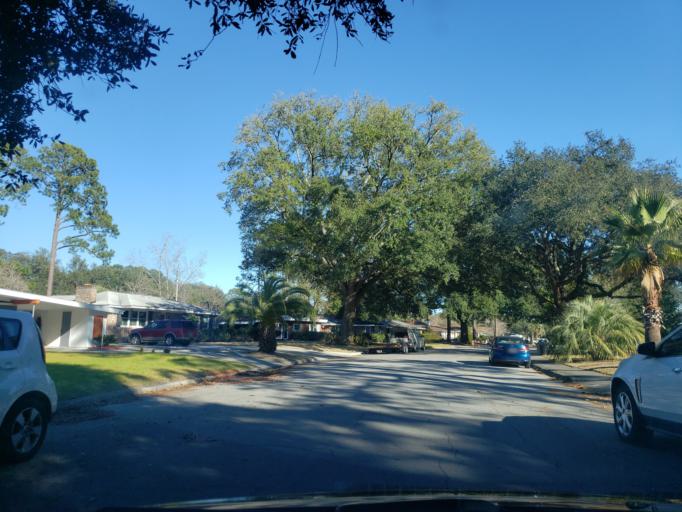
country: US
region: Georgia
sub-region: Chatham County
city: Thunderbolt
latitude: 32.0229
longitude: -81.1013
